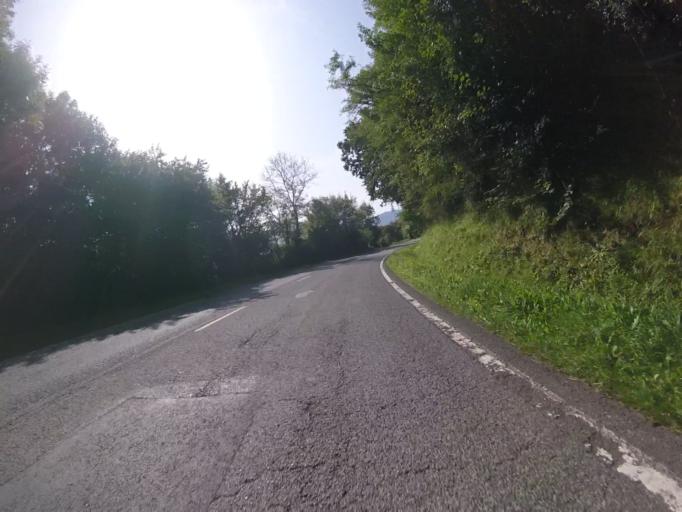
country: ES
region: Navarre
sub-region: Provincia de Navarra
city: Zugarramurdi
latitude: 43.2250
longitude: -1.4913
